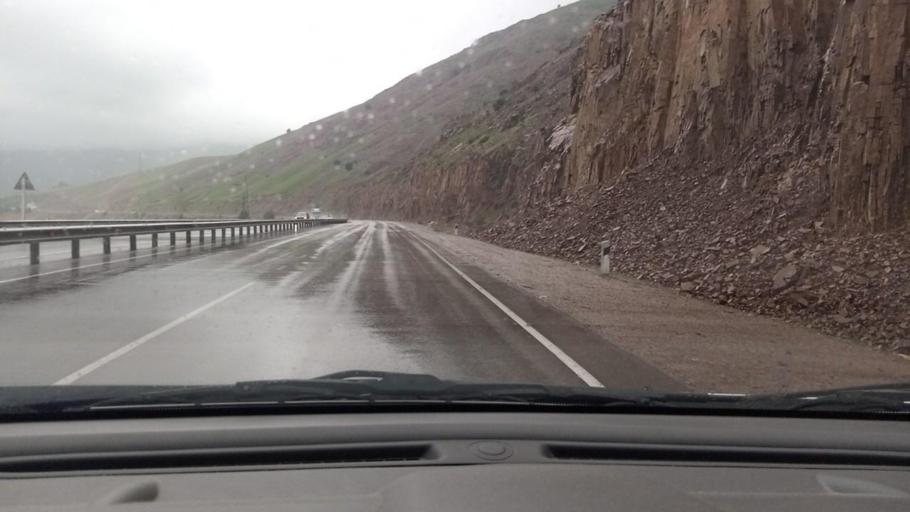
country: UZ
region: Toshkent
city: Angren
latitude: 41.1182
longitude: 70.3462
